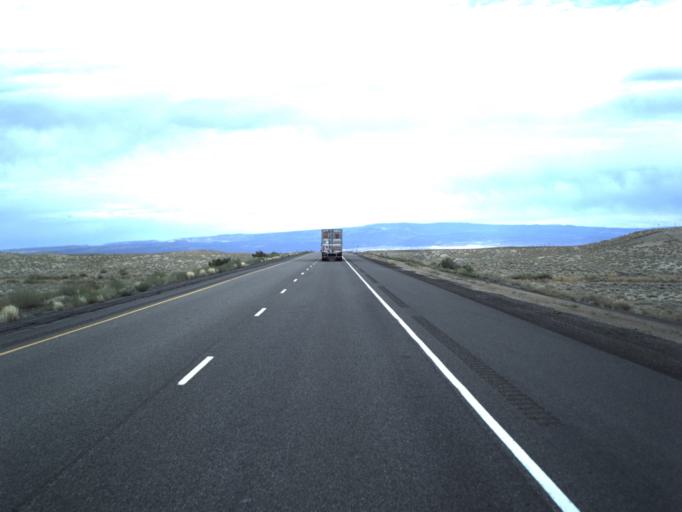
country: US
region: Utah
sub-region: Grand County
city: Moab
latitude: 38.9384
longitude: -109.4983
